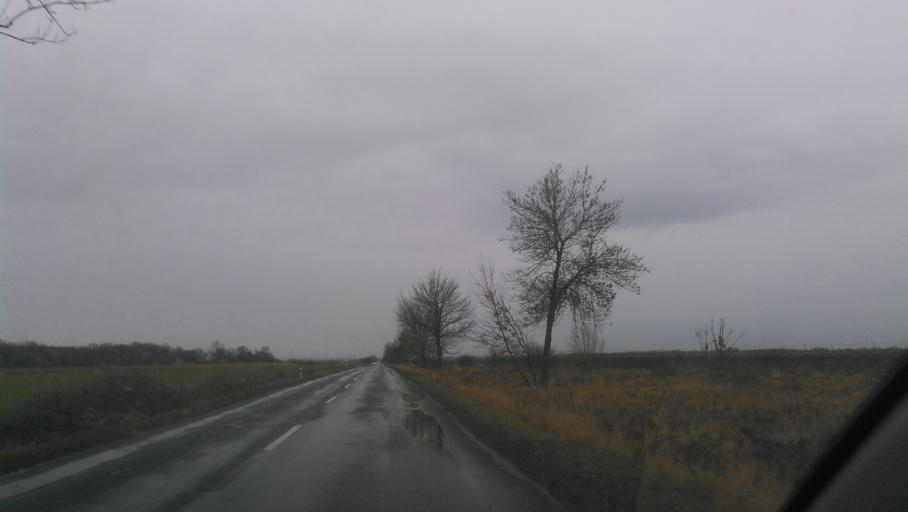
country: SK
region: Nitriansky
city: Sellye
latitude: 48.1050
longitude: 17.8977
